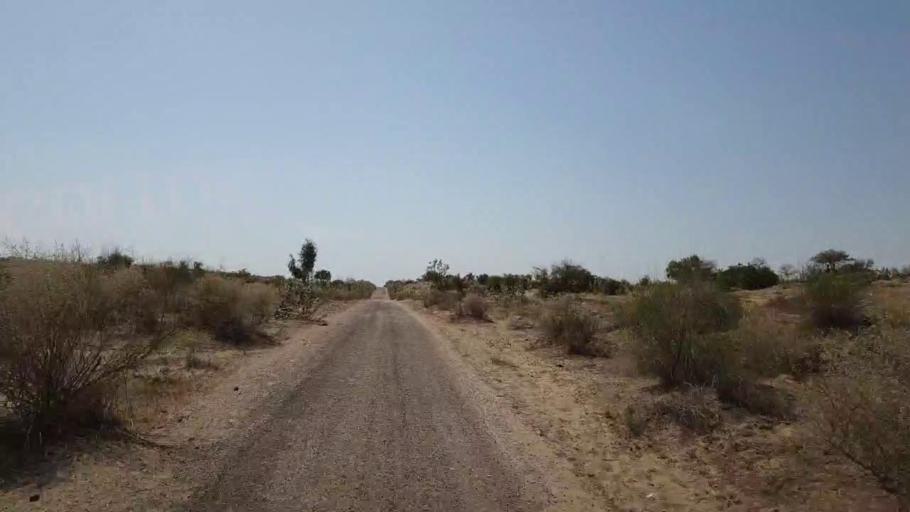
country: PK
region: Sindh
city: Umarkot
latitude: 25.1800
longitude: 69.8774
